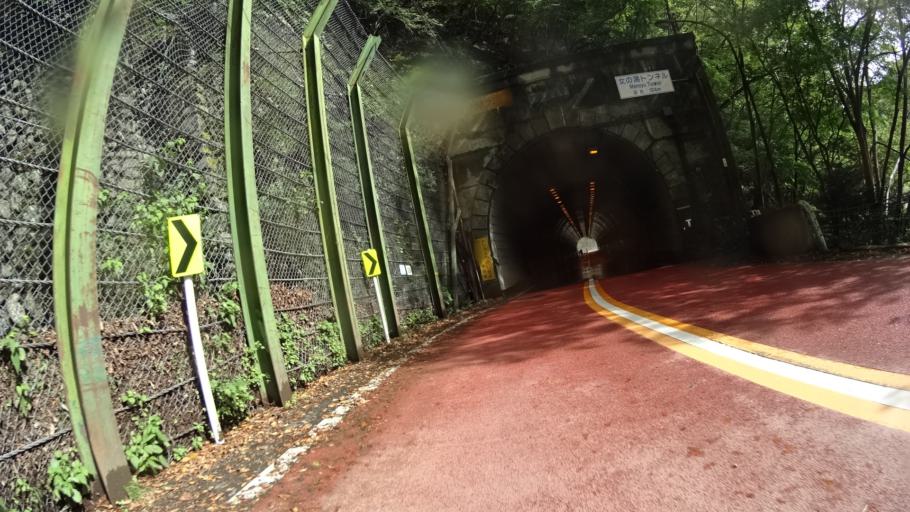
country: JP
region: Yamanashi
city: Uenohara
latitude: 35.7817
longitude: 139.0254
